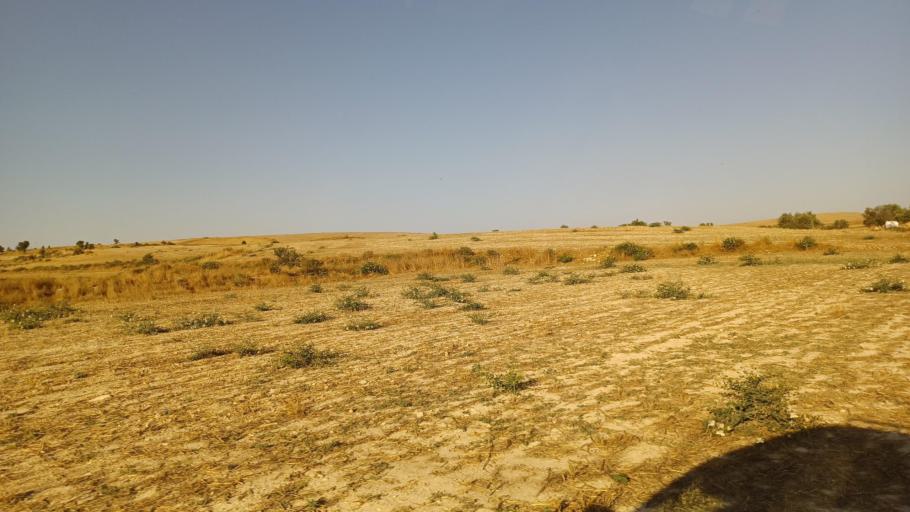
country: CY
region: Larnaka
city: Athienou
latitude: 35.0419
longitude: 33.5167
